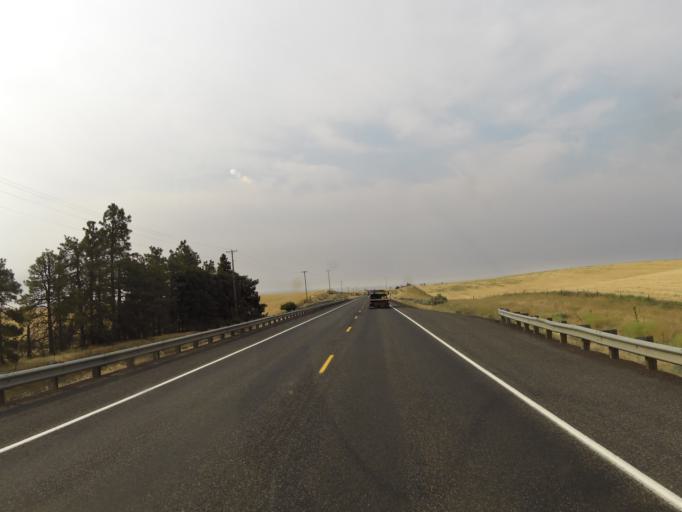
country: US
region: Oregon
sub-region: Sherman County
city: Moro
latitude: 45.3982
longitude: -120.7895
